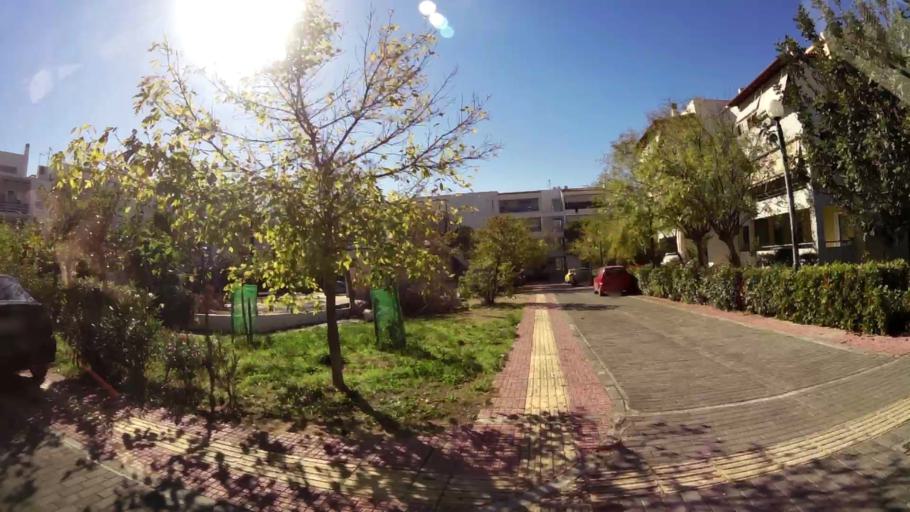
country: GR
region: Attica
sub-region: Nomarchia Anatolikis Attikis
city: Varybobi
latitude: 38.1086
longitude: 23.7710
